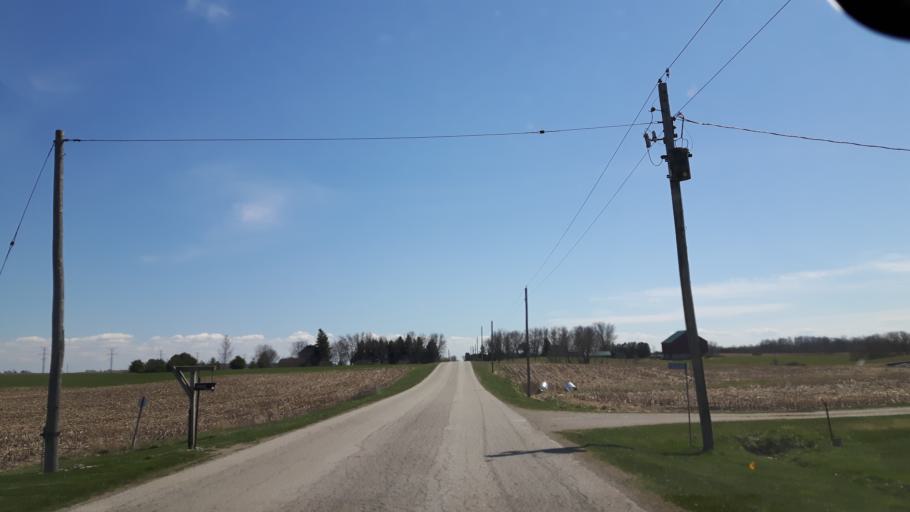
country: CA
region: Ontario
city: Goderich
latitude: 43.6292
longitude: -81.6440
